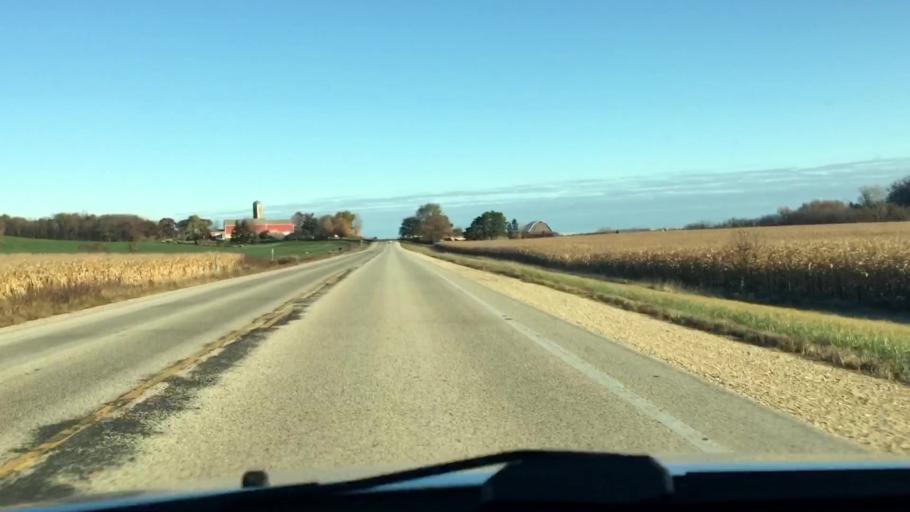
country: US
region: Wisconsin
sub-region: Dodge County
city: Theresa
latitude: 43.4432
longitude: -88.4504
